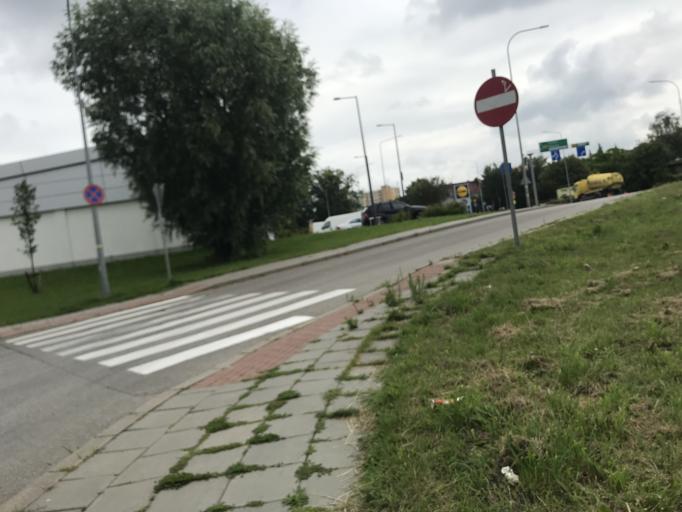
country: PL
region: Warmian-Masurian Voivodeship
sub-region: Powiat elblaski
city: Elblag
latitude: 54.1748
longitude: 19.3913
